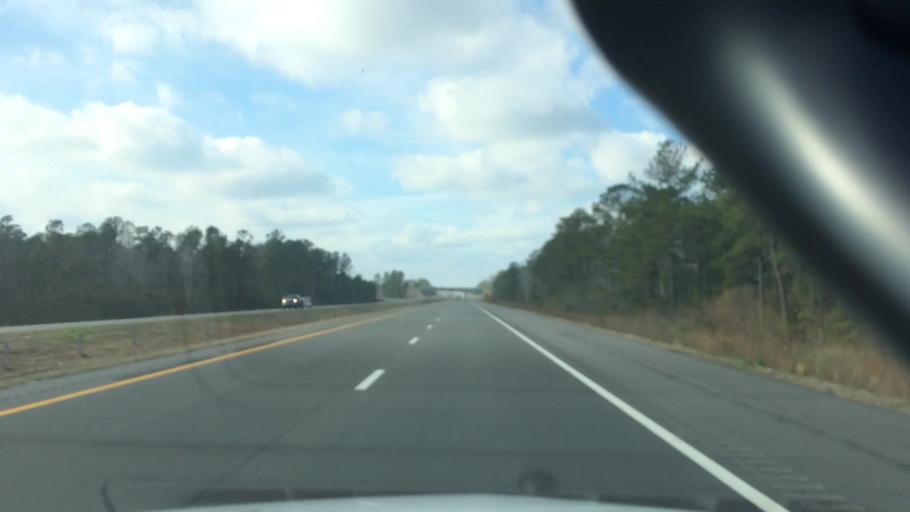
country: US
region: North Carolina
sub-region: Brunswick County
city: Leland
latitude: 34.2758
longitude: -78.0409
